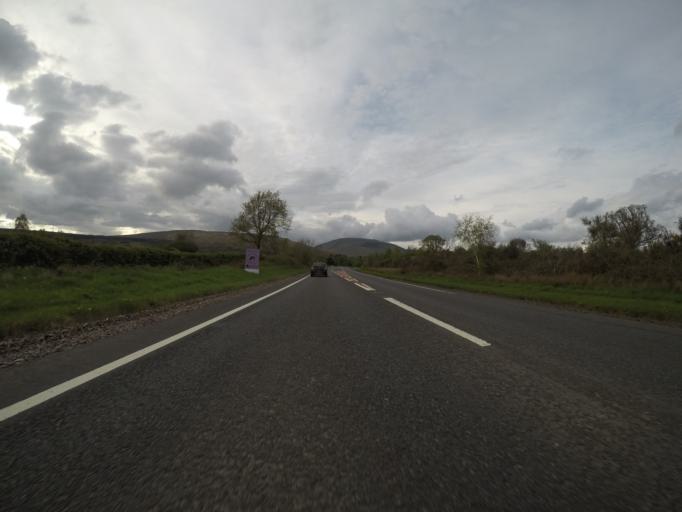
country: GB
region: Scotland
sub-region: West Dunbartonshire
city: Balloch
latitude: 56.0371
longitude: -4.6423
